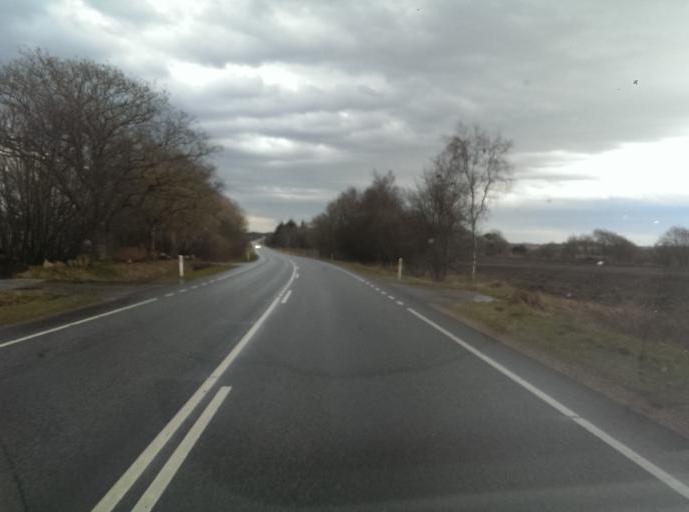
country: DK
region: South Denmark
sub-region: Esbjerg Kommune
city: Tjaereborg
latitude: 55.5063
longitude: 8.5996
